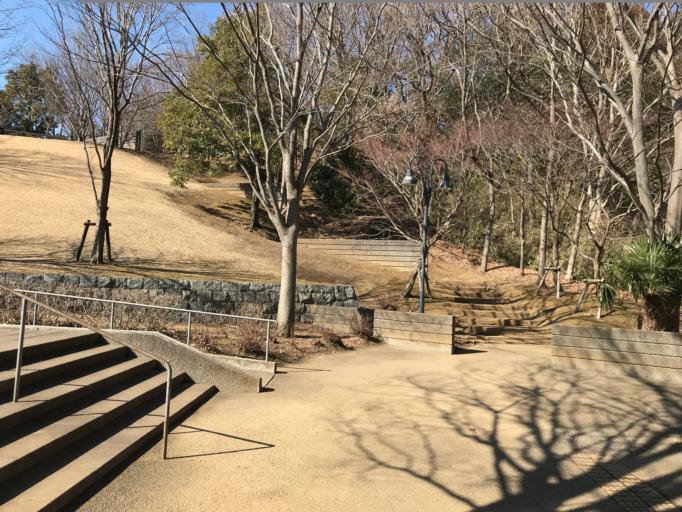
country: JP
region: Tokyo
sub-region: Machida-shi
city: Machida
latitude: 35.6085
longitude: 139.4658
